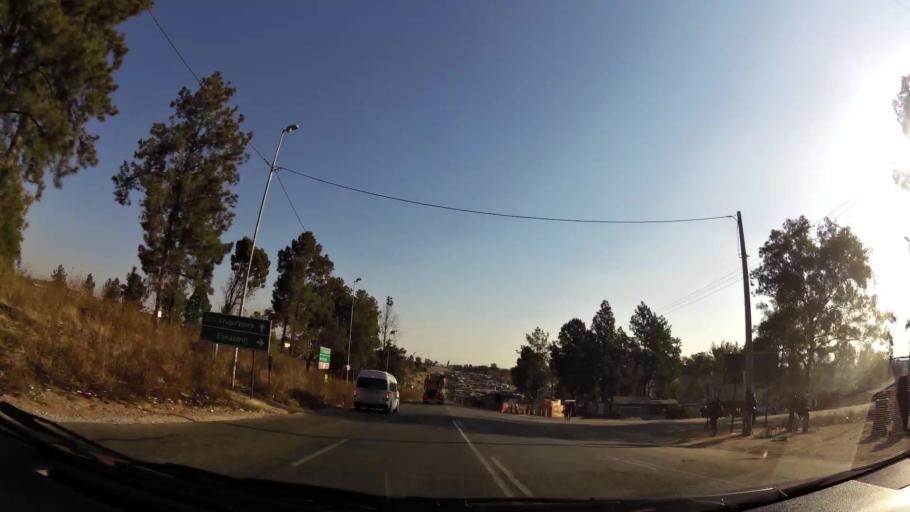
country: ZA
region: Gauteng
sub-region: West Rand District Municipality
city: Muldersdriseloop
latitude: -26.0202
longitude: 27.8795
